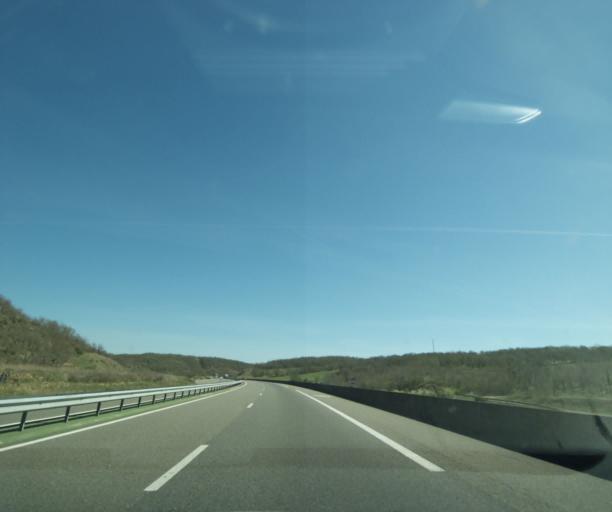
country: FR
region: Midi-Pyrenees
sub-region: Departement du Lot
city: Lalbenque
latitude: 44.4161
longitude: 1.5141
